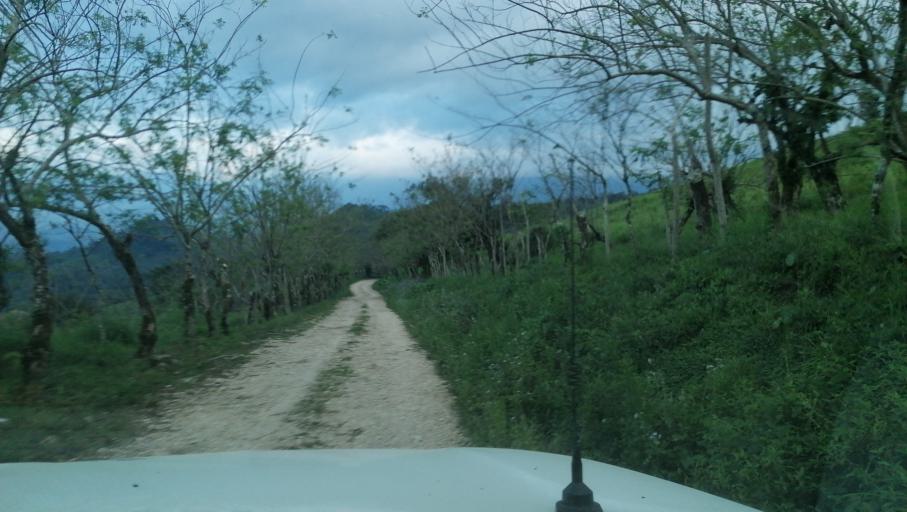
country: MX
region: Chiapas
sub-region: Francisco Leon
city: San Miguel la Sardina
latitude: 17.3019
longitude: -93.2659
